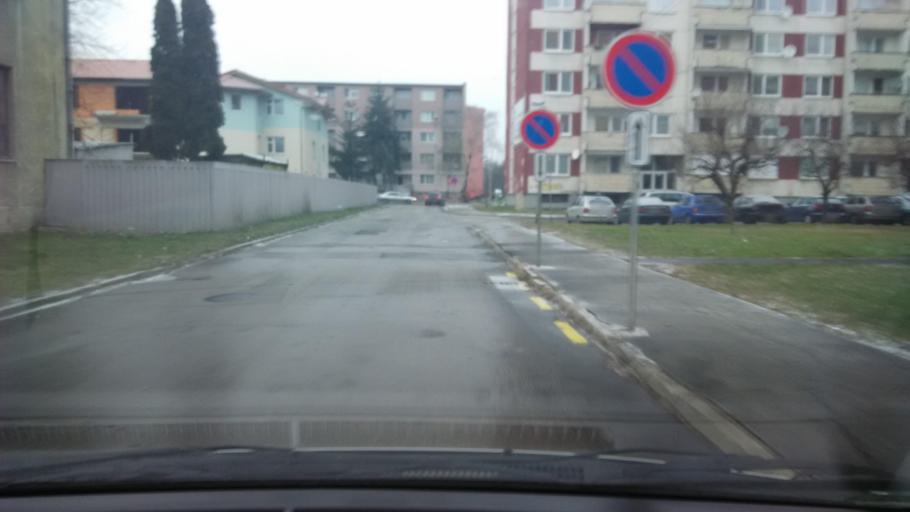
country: SK
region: Nitriansky
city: Levice
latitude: 48.2102
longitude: 18.6040
